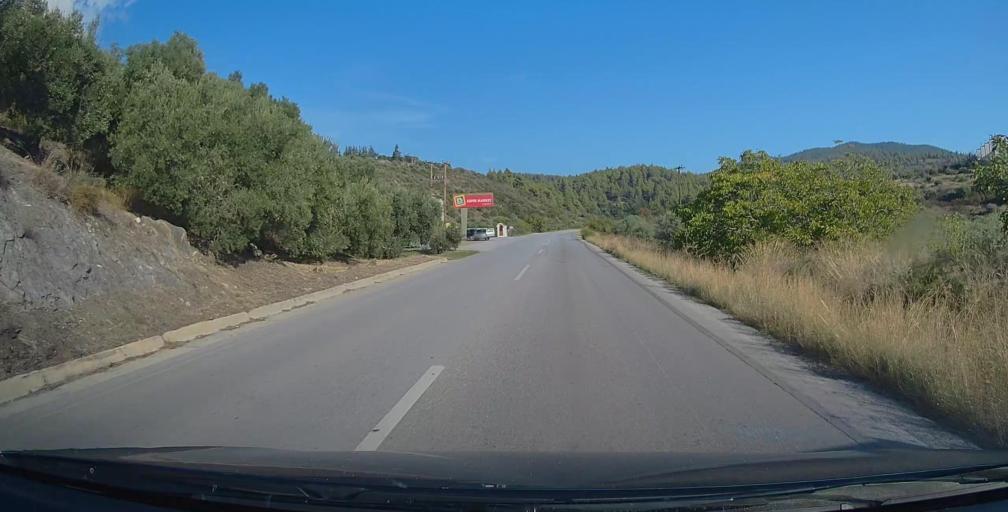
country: GR
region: Central Macedonia
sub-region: Nomos Chalkidikis
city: Neos Marmaras
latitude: 40.0860
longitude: 23.8056
